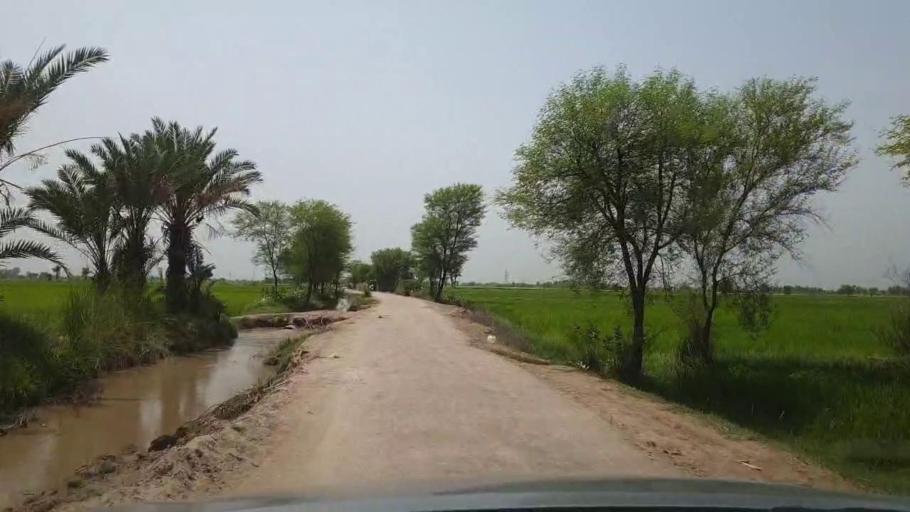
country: PK
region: Sindh
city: Madeji
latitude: 27.7808
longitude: 68.4323
